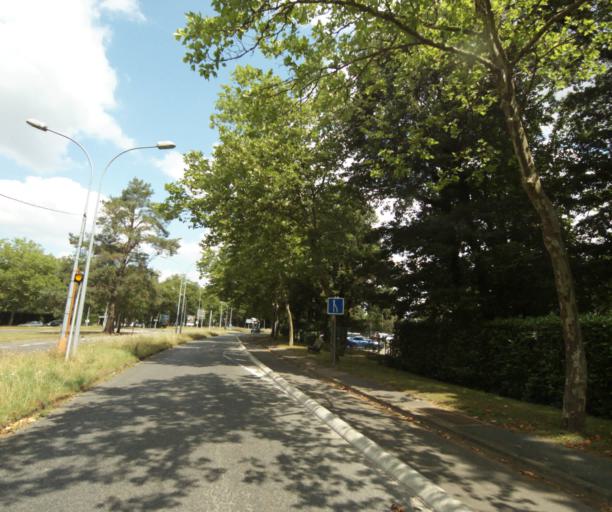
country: FR
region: Centre
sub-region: Departement du Loiret
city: Saint-Cyr-en-Val
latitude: 47.8280
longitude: 1.9366
